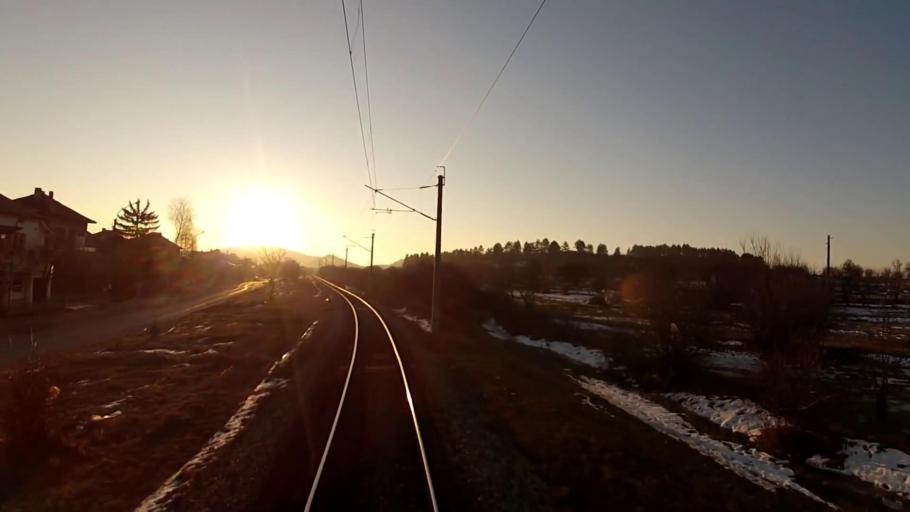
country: BG
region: Sofiya
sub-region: Obshtina Dragoman
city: Dragoman
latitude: 42.9138
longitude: 22.9379
